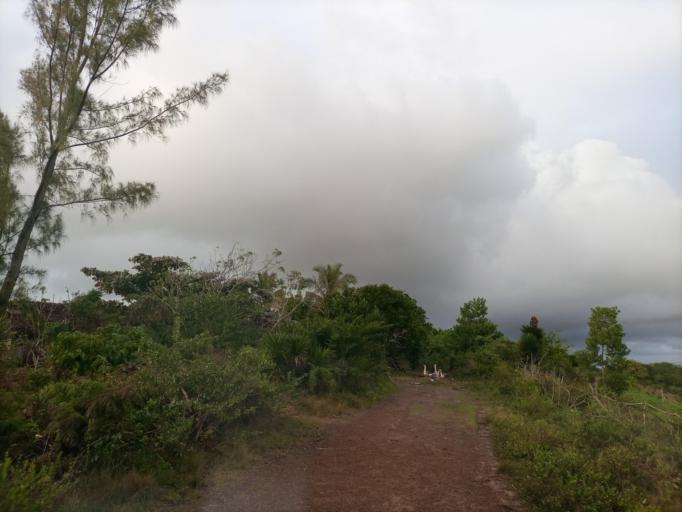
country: MG
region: Anosy
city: Fort Dauphin
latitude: -24.7015
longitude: 47.1782
